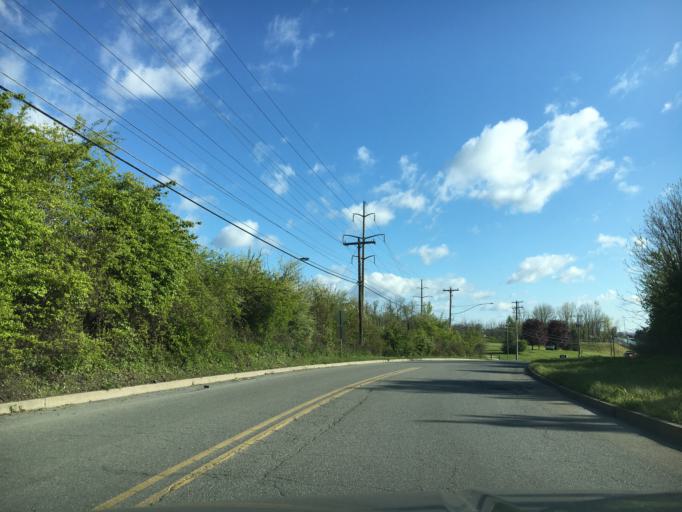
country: US
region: Pennsylvania
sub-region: Lehigh County
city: Stiles
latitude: 40.6721
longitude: -75.5071
